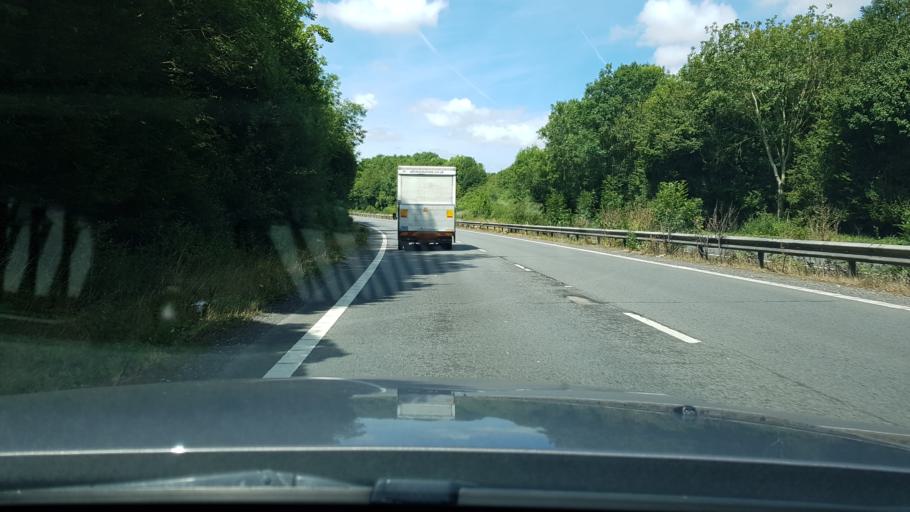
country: GB
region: England
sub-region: West Sussex
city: Chichester
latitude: 50.8426
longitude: -0.8088
